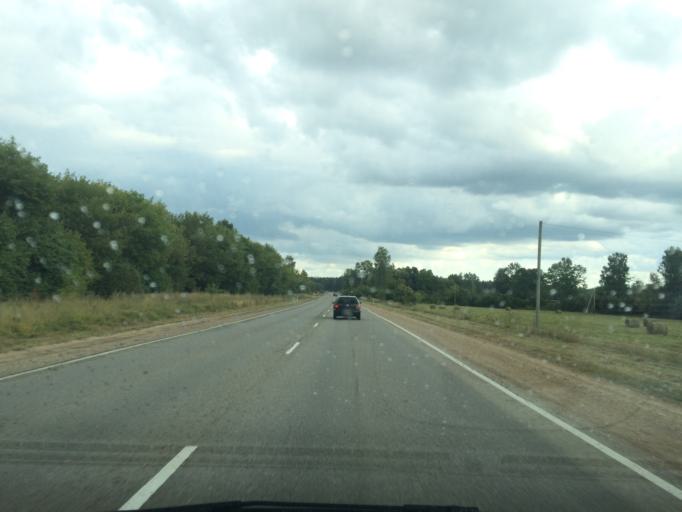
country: LV
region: Koknese
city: Koknese
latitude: 56.6055
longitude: 25.5092
